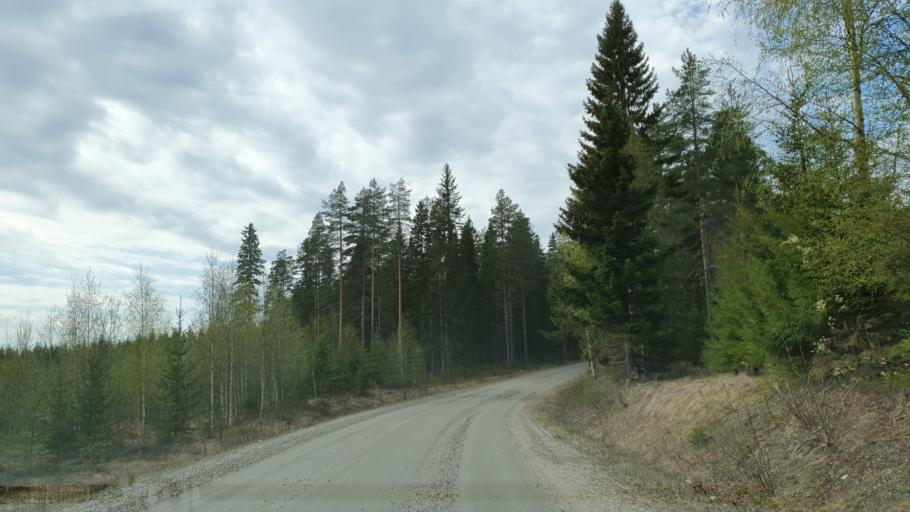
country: FI
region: Kainuu
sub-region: Kehys-Kainuu
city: Kuhmo
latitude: 64.0943
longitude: 29.8933
